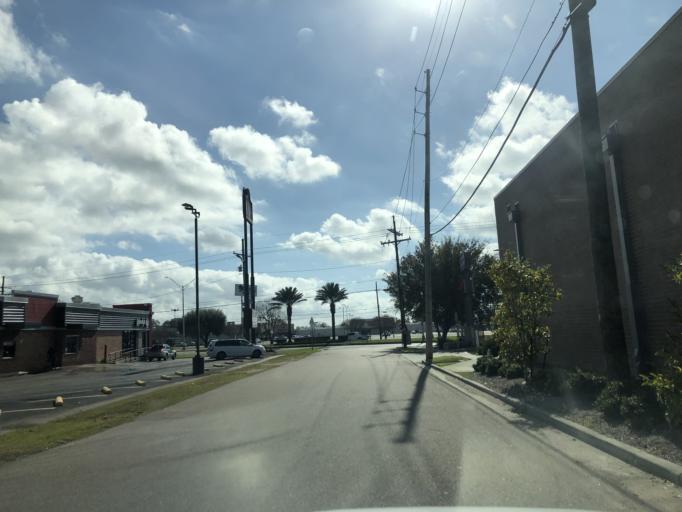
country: US
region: Louisiana
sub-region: Jefferson Parish
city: Kenner
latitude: 30.0060
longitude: -90.2193
